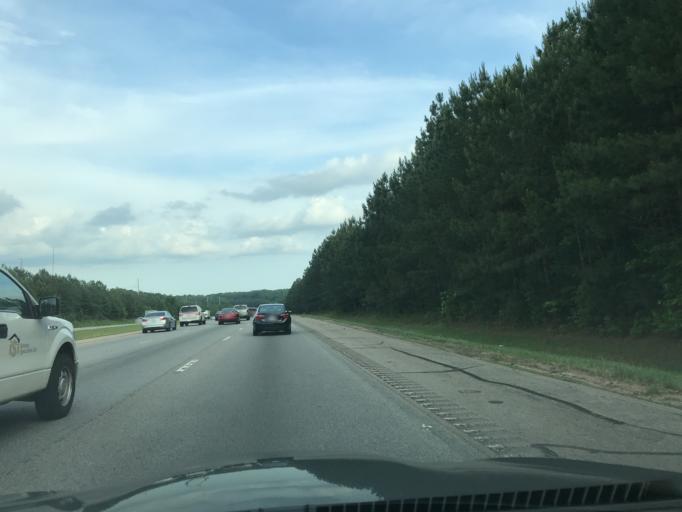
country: US
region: North Carolina
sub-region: Wake County
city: West Raleigh
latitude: 35.9064
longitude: -78.6384
